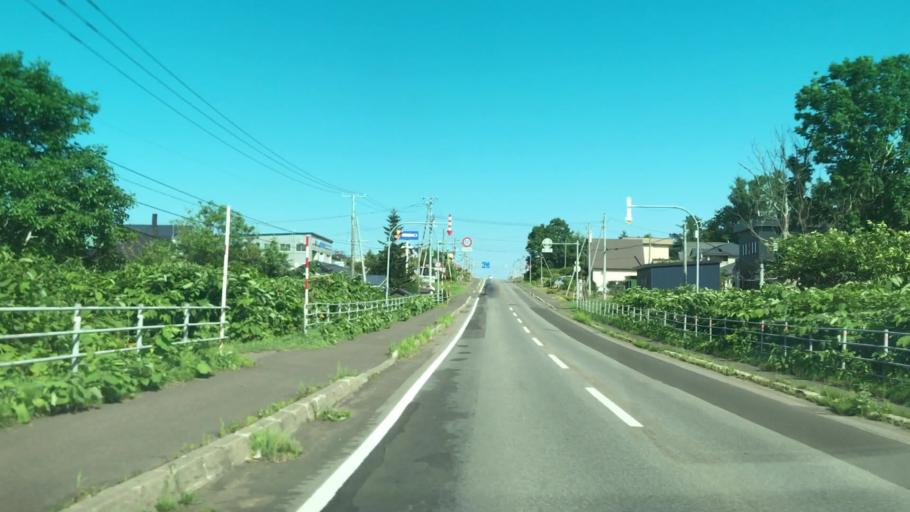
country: JP
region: Hokkaido
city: Iwanai
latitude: 42.9825
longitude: 140.5683
